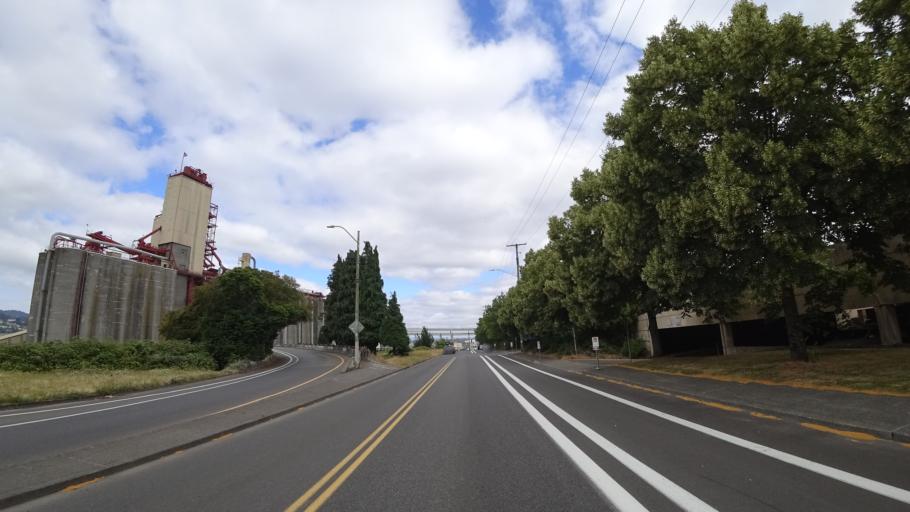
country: US
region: Oregon
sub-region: Multnomah County
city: Portland
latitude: 45.5349
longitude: -122.6728
